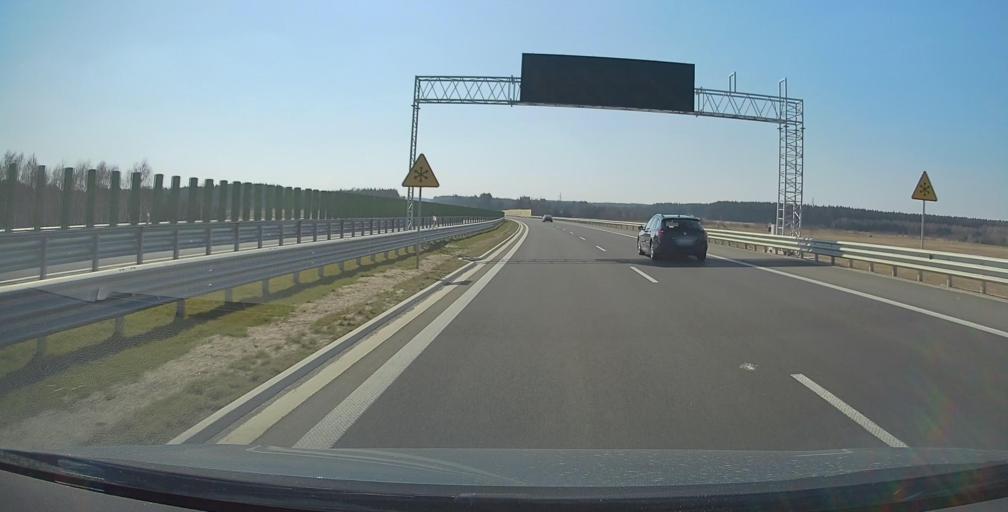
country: PL
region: Subcarpathian Voivodeship
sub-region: Powiat nizanski
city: Konczyce
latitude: 50.4630
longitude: 22.1414
